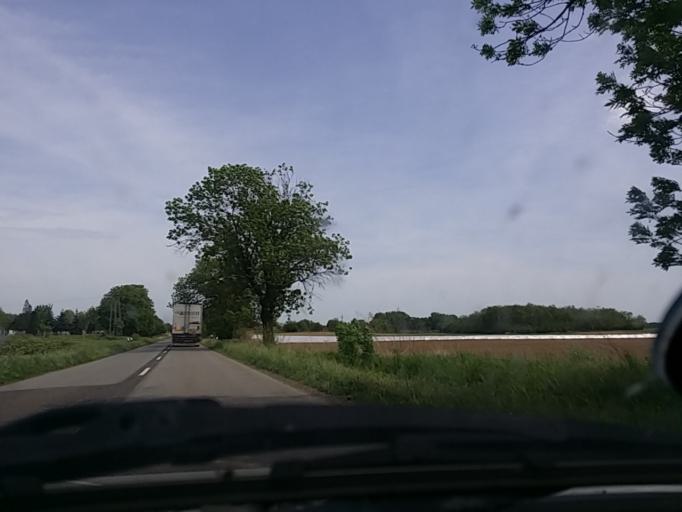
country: HU
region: Baranya
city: Vajszlo
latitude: 45.8643
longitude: 17.9718
